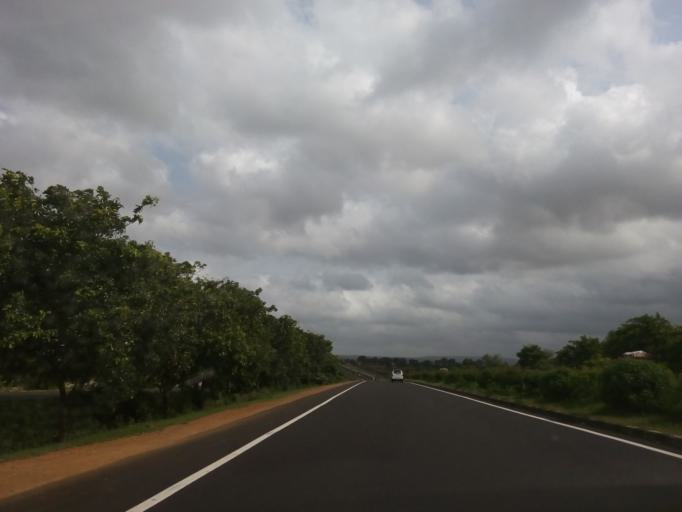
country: IN
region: Karnataka
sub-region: Belgaum
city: Hukeri
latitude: 16.1129
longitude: 74.5173
